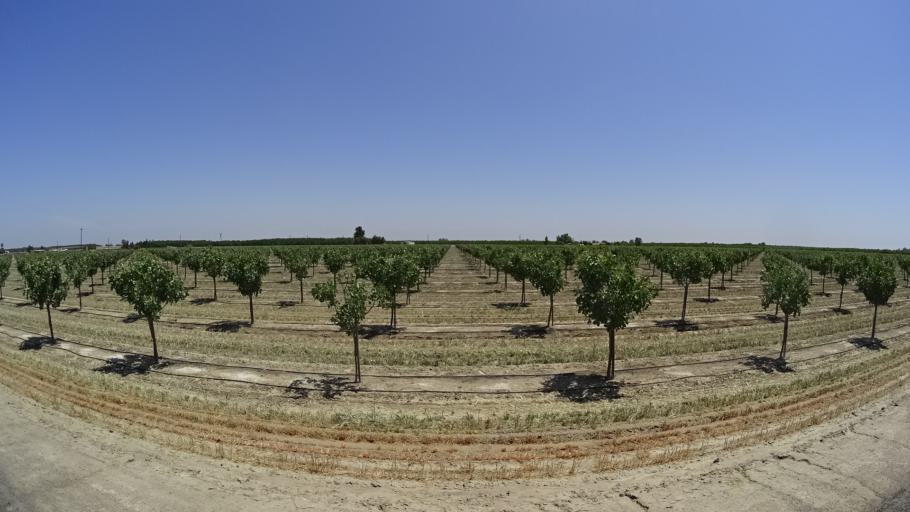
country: US
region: California
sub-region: Kings County
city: Lemoore
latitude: 36.2898
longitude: -119.7628
